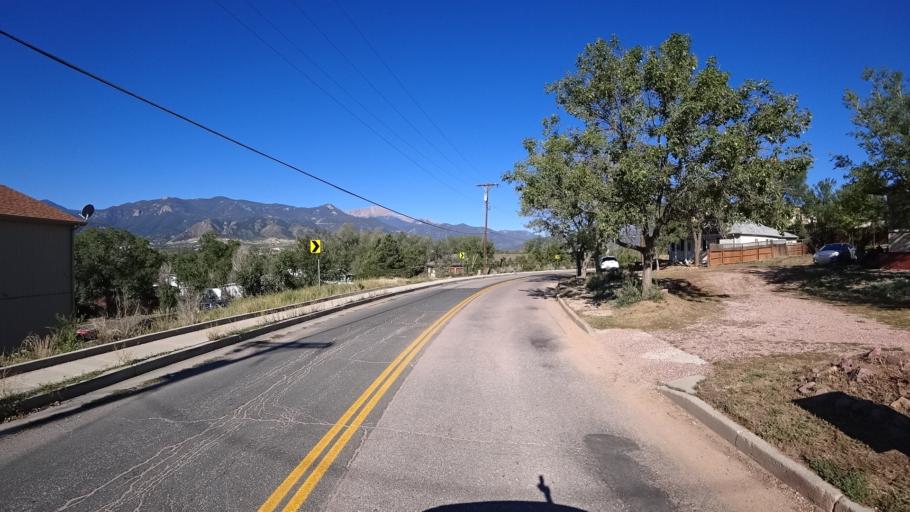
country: US
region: Colorado
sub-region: El Paso County
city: Colorado Springs
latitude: 38.8454
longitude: -104.8435
